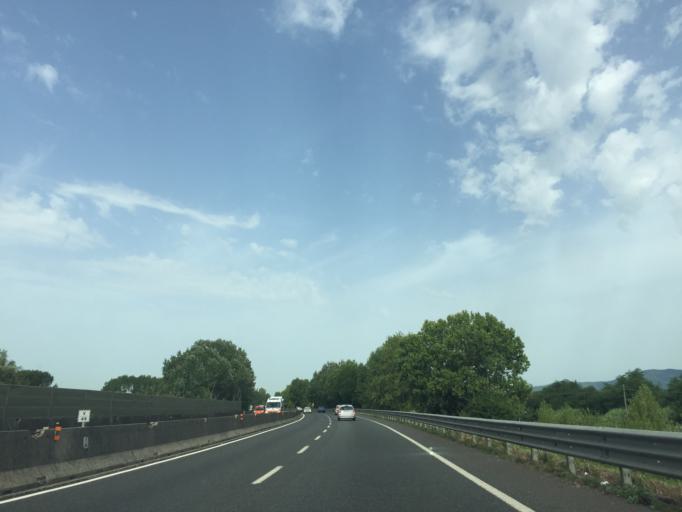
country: IT
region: Tuscany
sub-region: Province of Pisa
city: La Rotta
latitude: 43.6552
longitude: 10.6694
